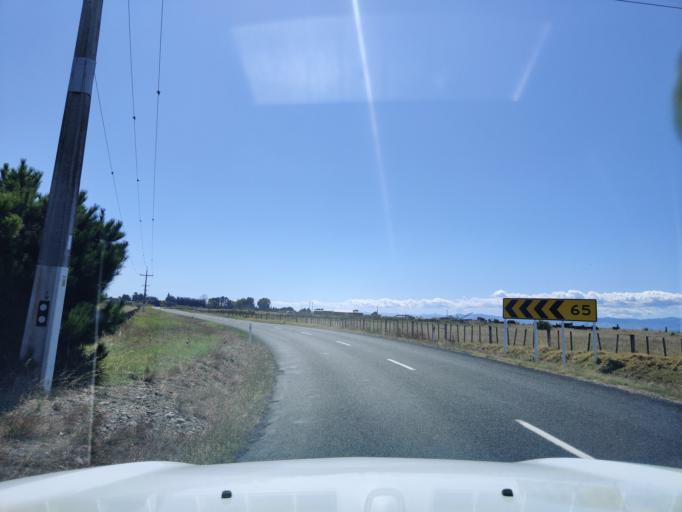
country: NZ
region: Waikato
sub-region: Thames-Coromandel District
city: Thames
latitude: -37.0645
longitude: 175.2983
